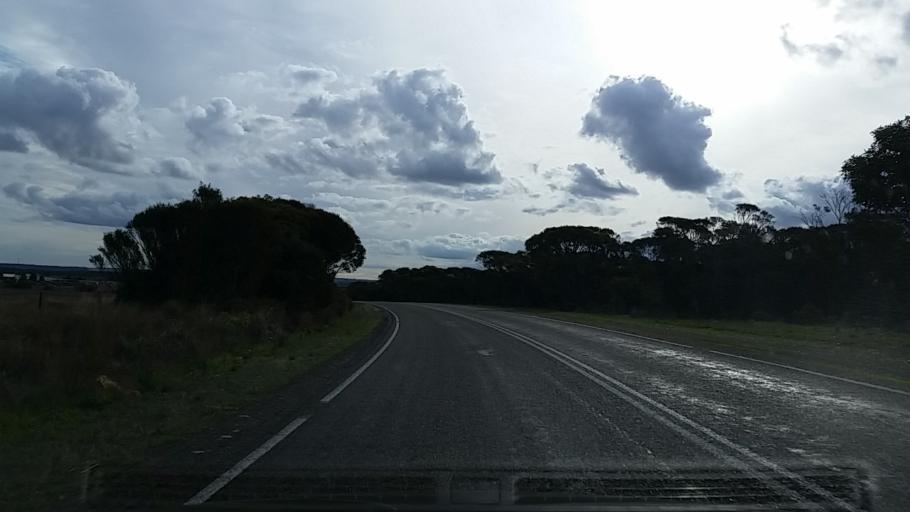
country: AU
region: South Australia
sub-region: Murray Bridge
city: Murray Bridge
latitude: -35.1257
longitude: 139.1880
